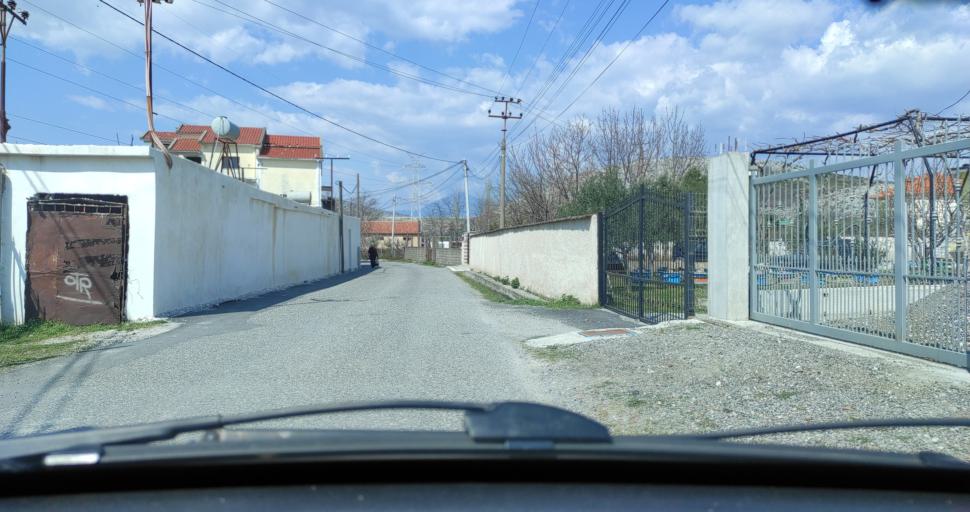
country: AL
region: Shkoder
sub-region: Rrethi i Shkodres
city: Vau i Dejes
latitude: 42.0063
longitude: 19.6419
